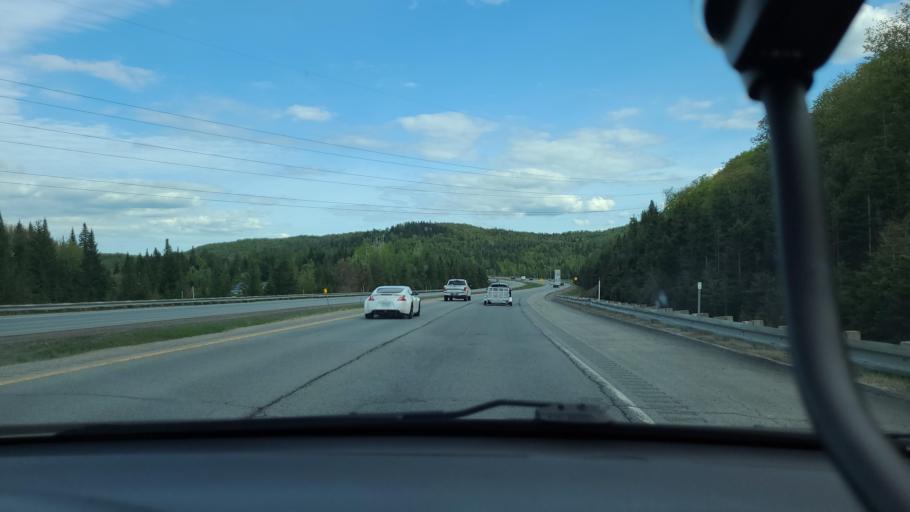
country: CA
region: Quebec
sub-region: Laurentides
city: Sainte-Agathe-des-Monts
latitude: 46.0314
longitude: -74.2653
